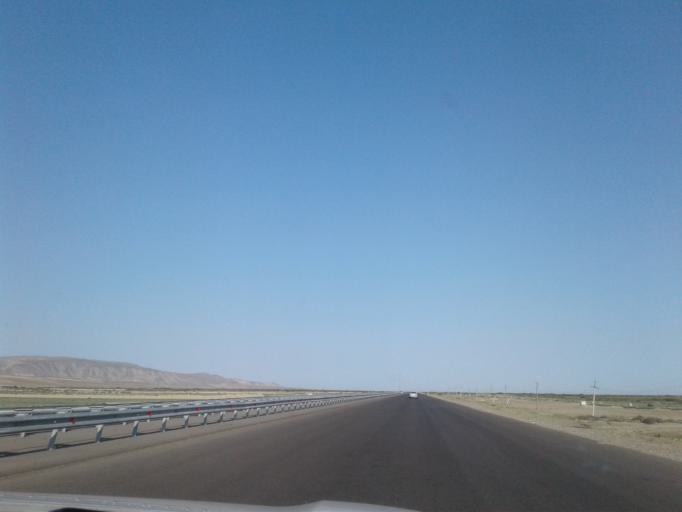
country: TM
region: Balkan
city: Serdar
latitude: 38.8995
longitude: 56.5138
